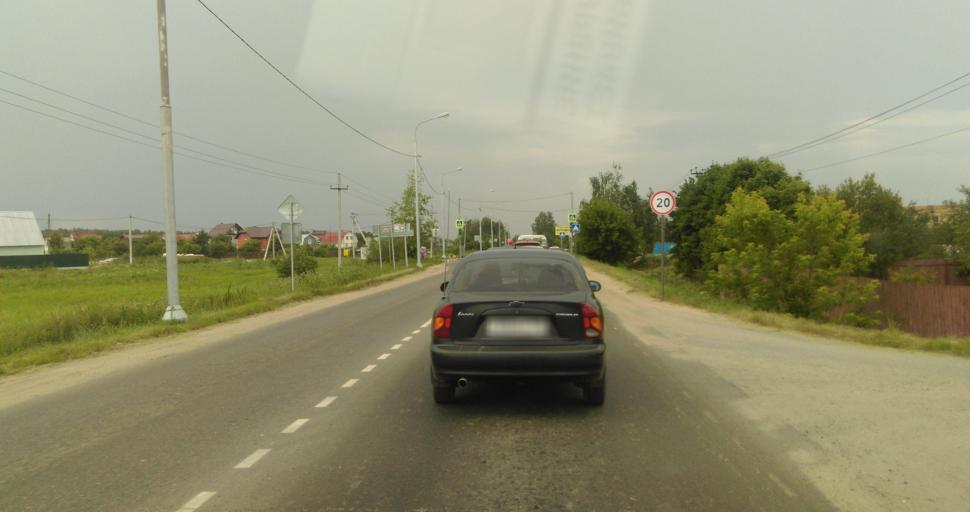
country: RU
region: Moskovskaya
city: Zhitnevo
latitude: 55.3386
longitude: 37.9090
